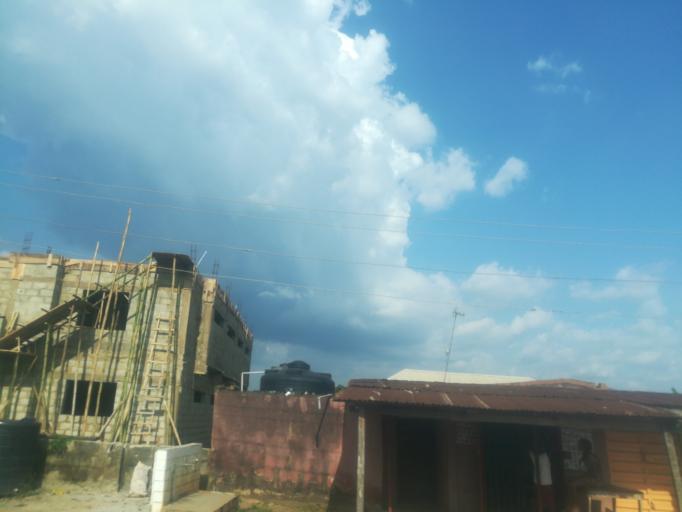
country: NG
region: Oyo
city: Ibadan
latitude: 7.4134
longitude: 3.8353
